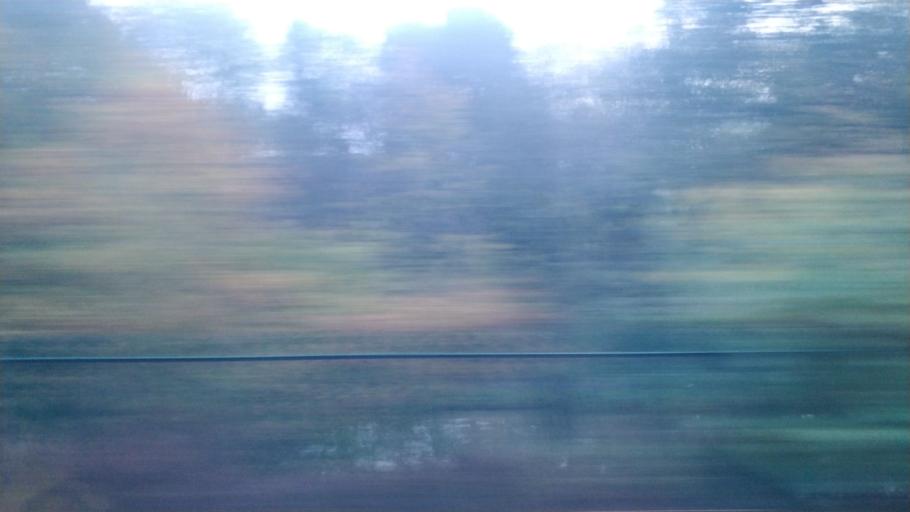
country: GB
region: England
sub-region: Lancashire
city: Parbold
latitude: 53.5853
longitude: -2.7479
